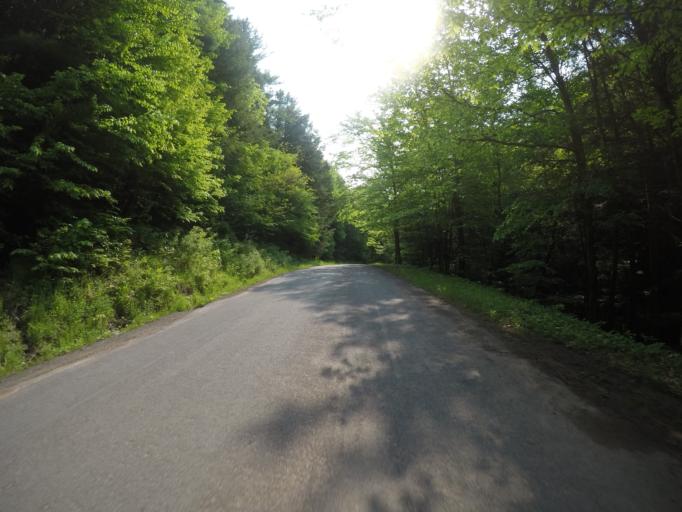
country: US
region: New York
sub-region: Sullivan County
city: Livingston Manor
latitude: 42.0770
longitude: -74.7722
